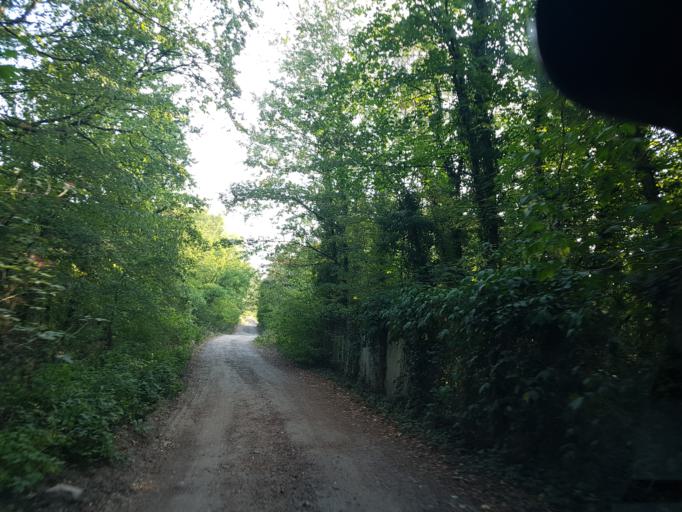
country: DE
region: Saxony-Anhalt
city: Coswig
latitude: 51.8966
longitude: 12.4379
